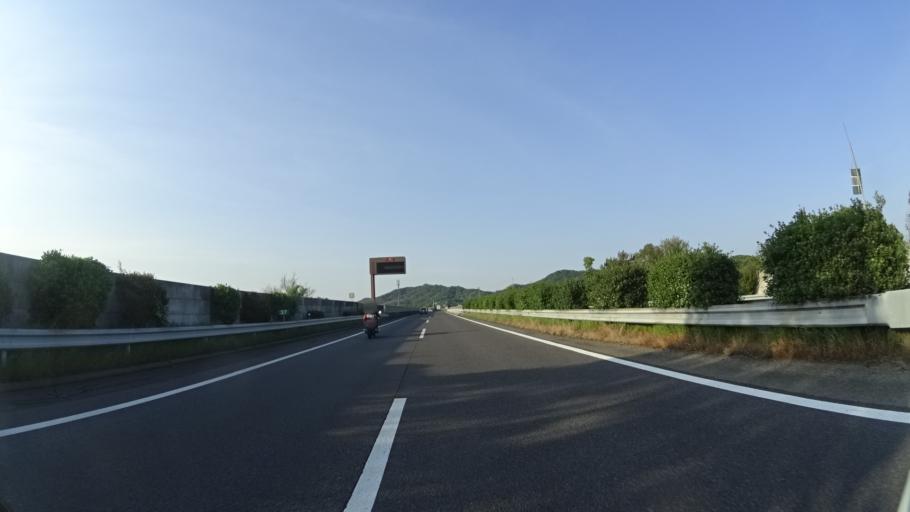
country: JP
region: Kagawa
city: Kan'onjicho
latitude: 34.1429
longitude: 133.7124
